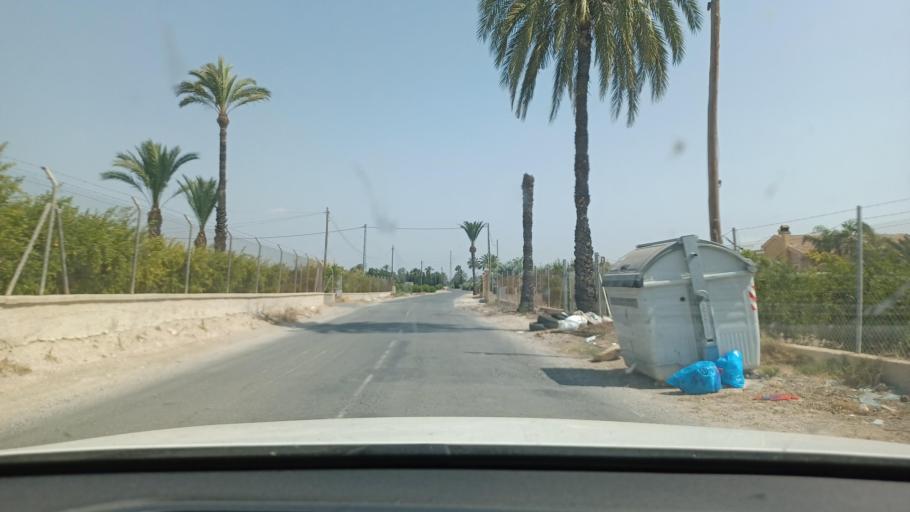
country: ES
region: Valencia
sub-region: Provincia de Alicante
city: Elche
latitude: 38.2256
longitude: -0.6948
